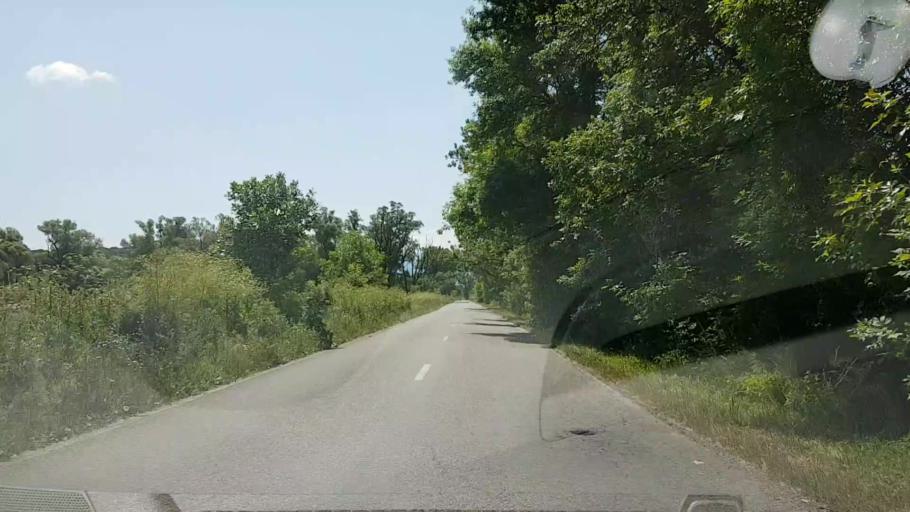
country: RO
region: Brasov
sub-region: Comuna Voila
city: Voila
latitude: 45.8569
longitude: 24.8289
